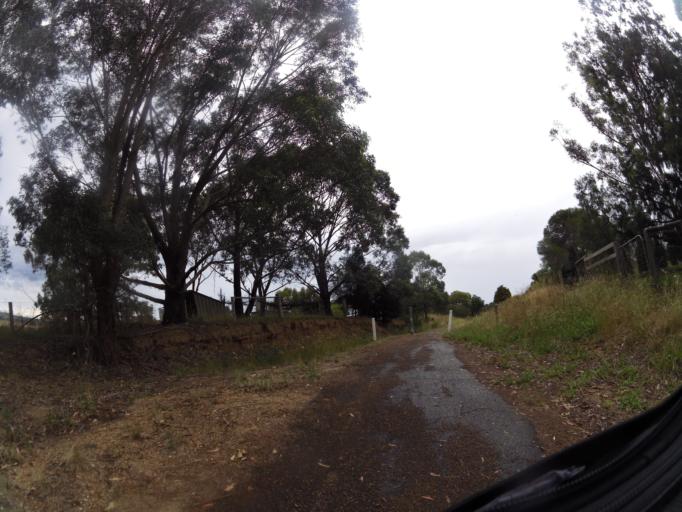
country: AU
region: Victoria
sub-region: East Gippsland
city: Bairnsdale
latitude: -37.7119
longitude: 147.8107
